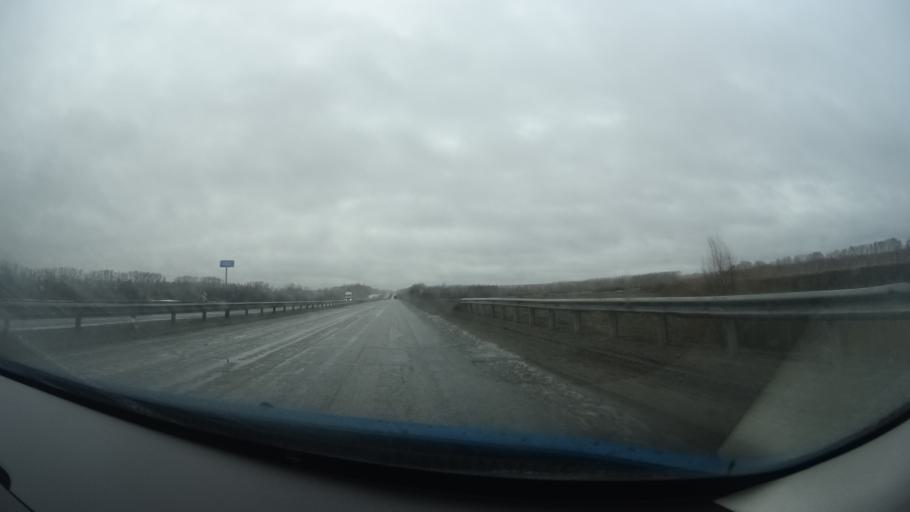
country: RU
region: Bashkortostan
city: Dmitriyevka
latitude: 54.7101
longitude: 55.2200
